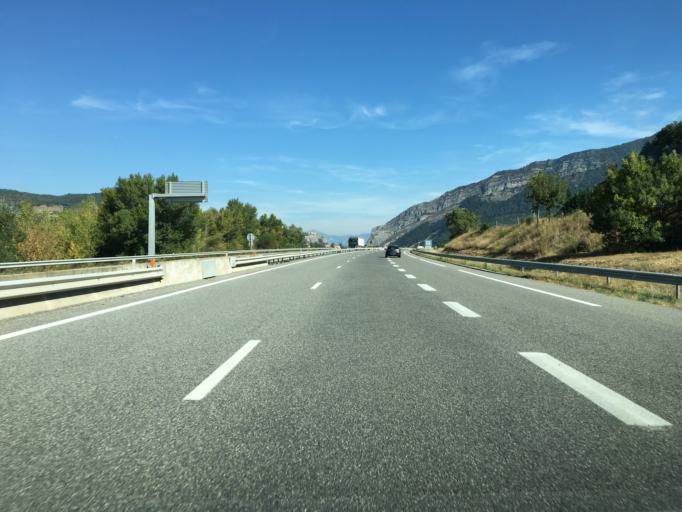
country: FR
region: Provence-Alpes-Cote d'Azur
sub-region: Departement des Alpes-de-Haute-Provence
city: Sisteron
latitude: 44.1725
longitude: 5.9542
